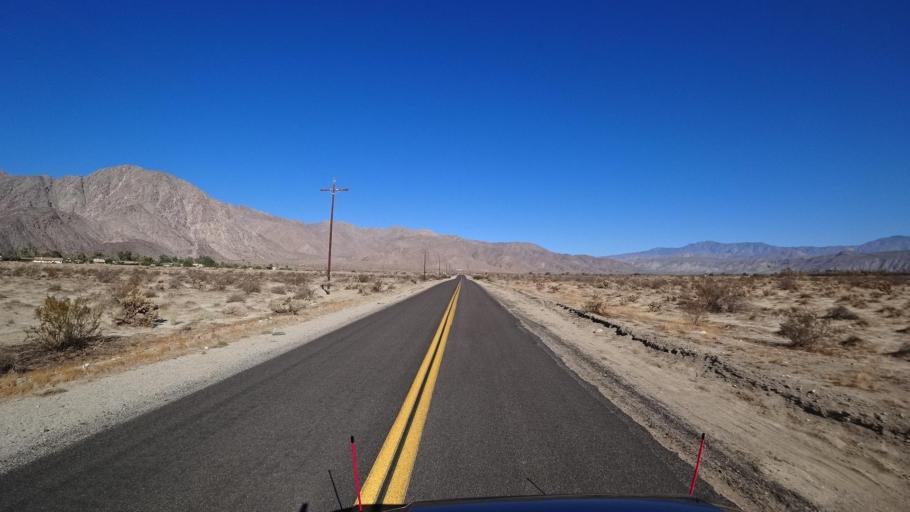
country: US
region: California
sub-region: San Diego County
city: Borrego Springs
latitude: 33.2948
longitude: -116.3800
